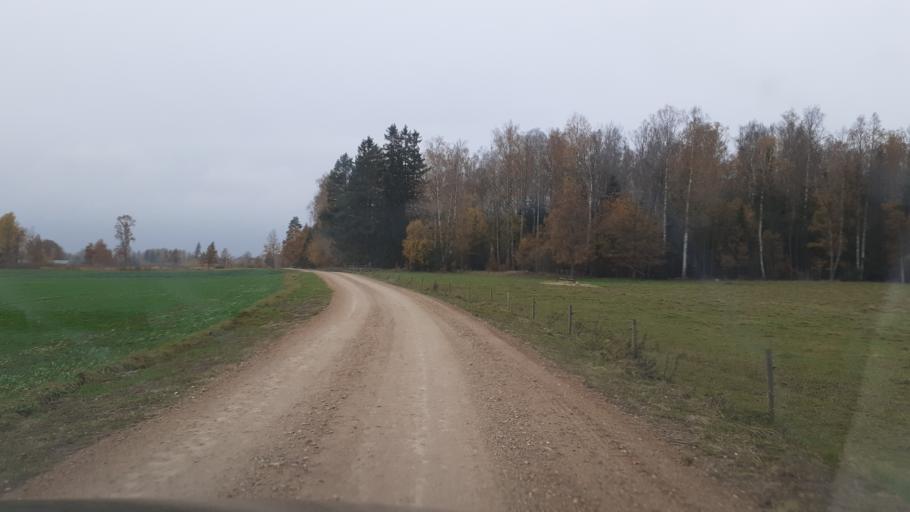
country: LV
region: Saldus Rajons
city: Saldus
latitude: 56.8723
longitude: 22.3293
